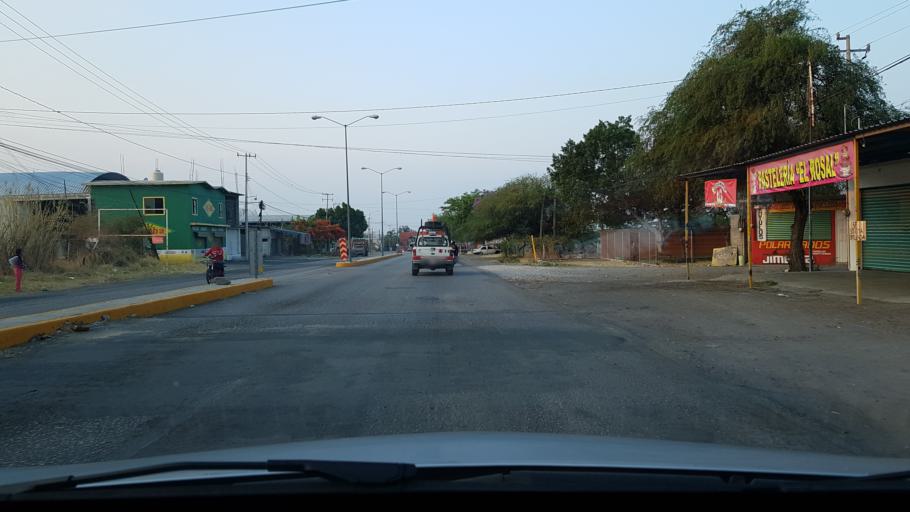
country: MX
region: Morelos
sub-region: Jonacatepec
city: Amacuitlapilco
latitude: 18.7029
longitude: -98.8009
